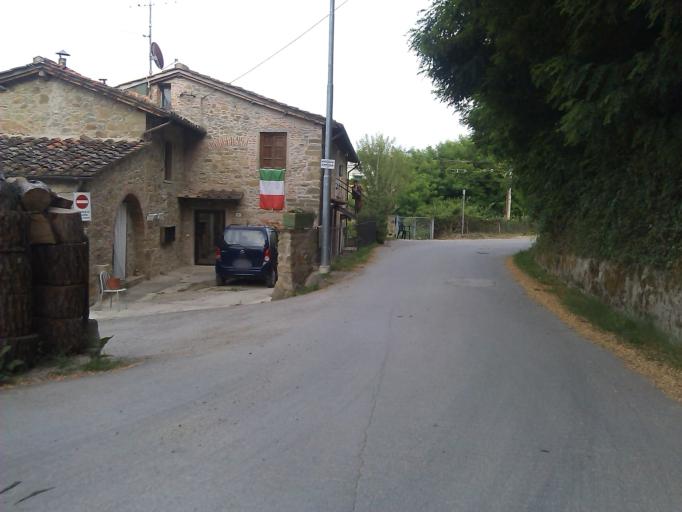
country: IT
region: Tuscany
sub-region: Province of Arezzo
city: Bucine
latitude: 43.4966
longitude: 11.6316
